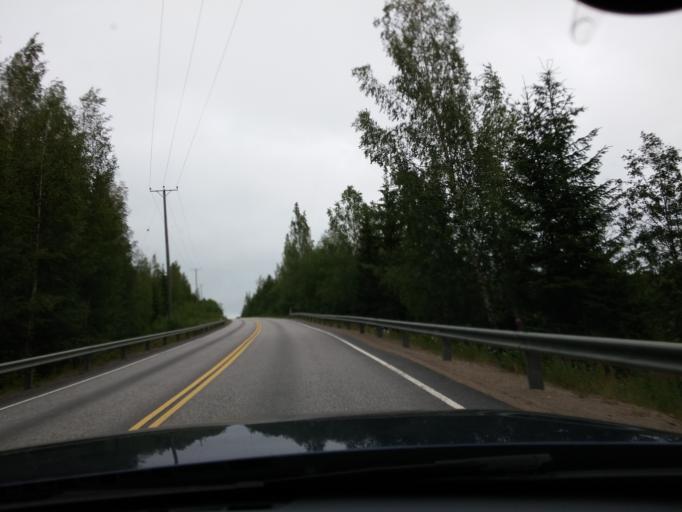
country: FI
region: Central Finland
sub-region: Joutsa
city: Luhanka
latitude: 61.9411
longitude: 25.7067
